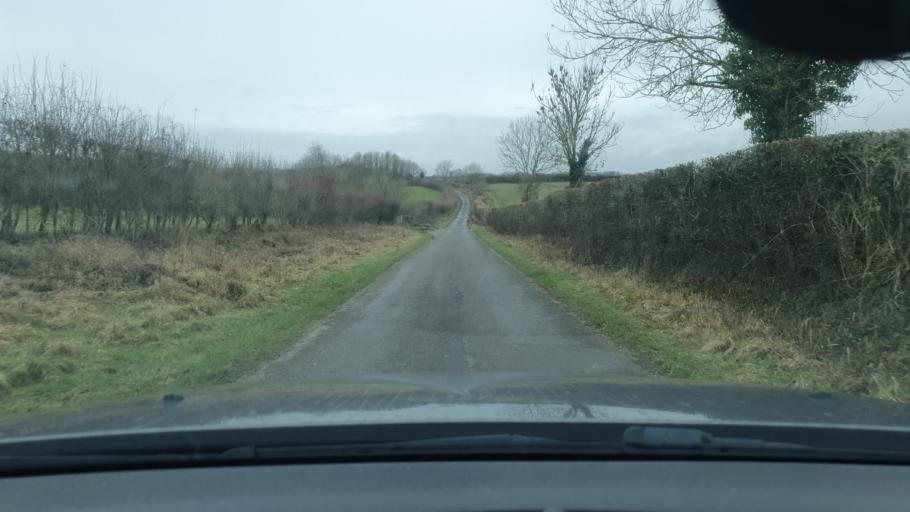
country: GB
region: England
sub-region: West Berkshire
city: Kintbury
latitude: 51.3968
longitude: -1.4285
